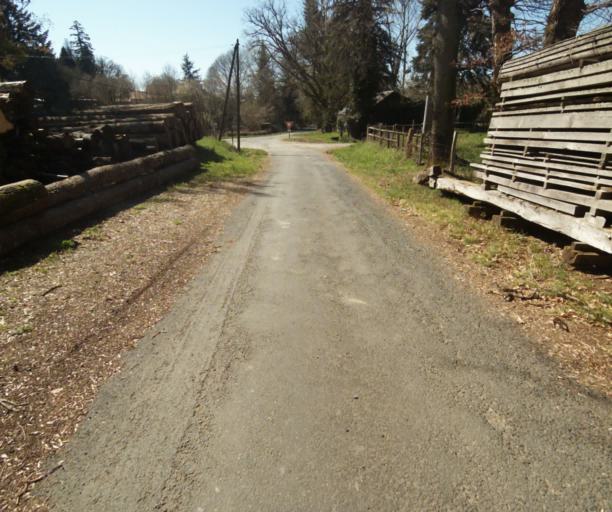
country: FR
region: Limousin
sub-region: Departement de la Correze
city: Saint-Clement
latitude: 45.3224
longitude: 1.6663
